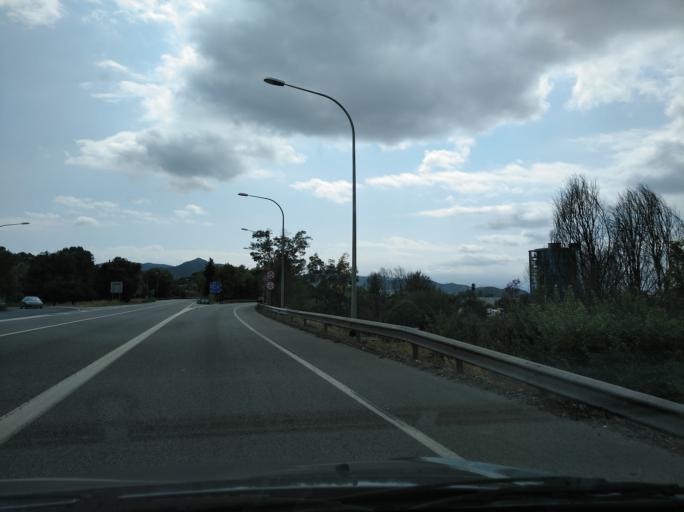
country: ES
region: Catalonia
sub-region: Provincia de Barcelona
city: Granollers
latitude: 41.5723
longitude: 2.2818
